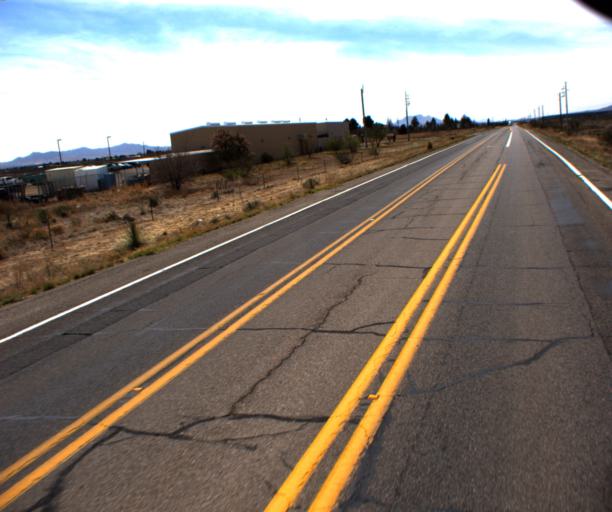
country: US
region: Arizona
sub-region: Cochise County
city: Pirtleville
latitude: 31.3732
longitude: -109.5794
